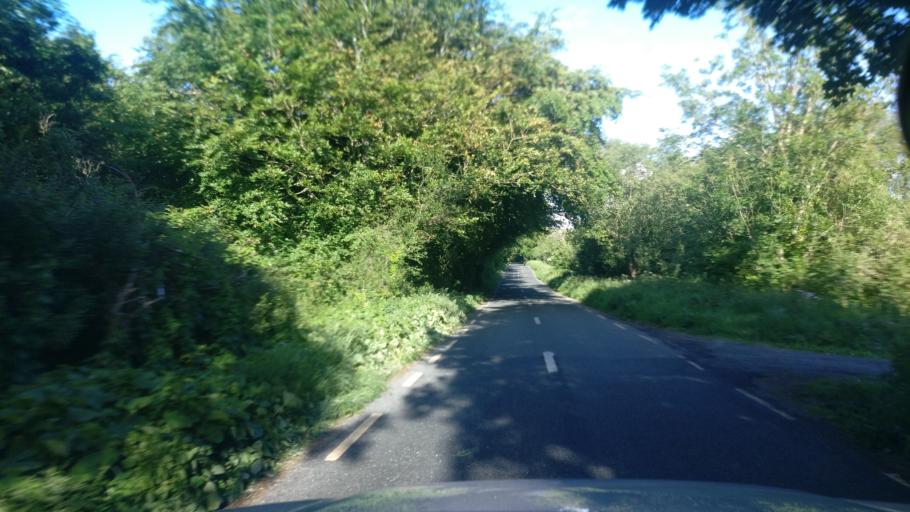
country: IE
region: Connaught
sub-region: County Galway
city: Ballinasloe
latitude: 53.2248
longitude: -8.2208
